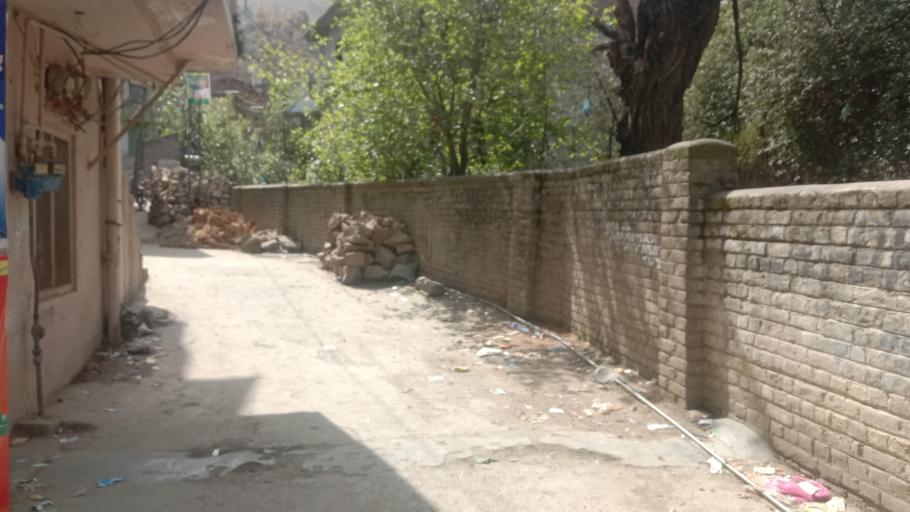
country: PK
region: Khyber Pakhtunkhwa
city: Abbottabad
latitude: 34.1309
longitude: 73.2002
